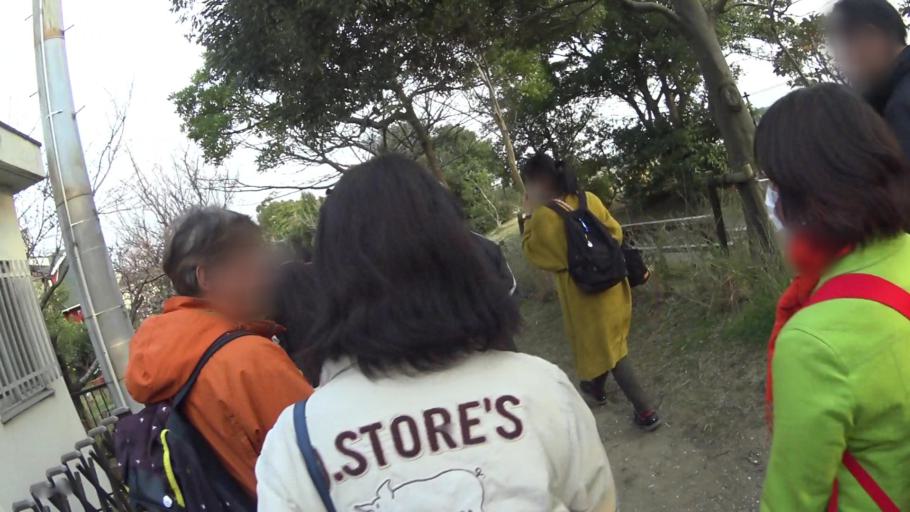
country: JP
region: Chiba
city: Funabashi
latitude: 35.6813
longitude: 140.0023
